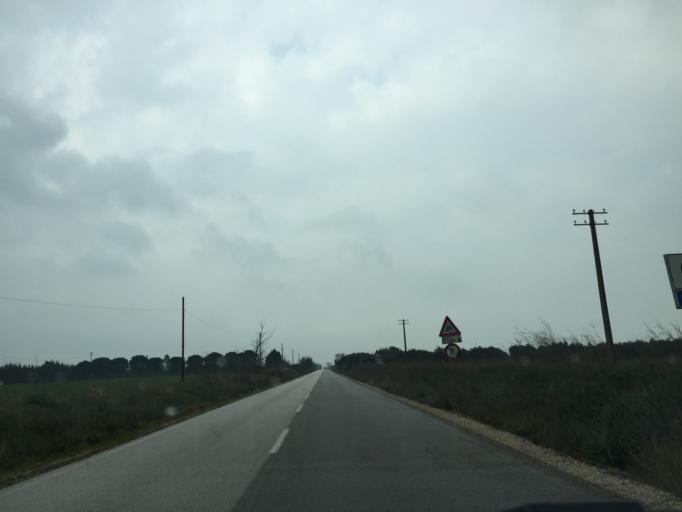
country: IT
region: Apulia
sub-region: Provincia di Foggia
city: Castelluccio dei Sauri
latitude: 41.4054
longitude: 15.4393
